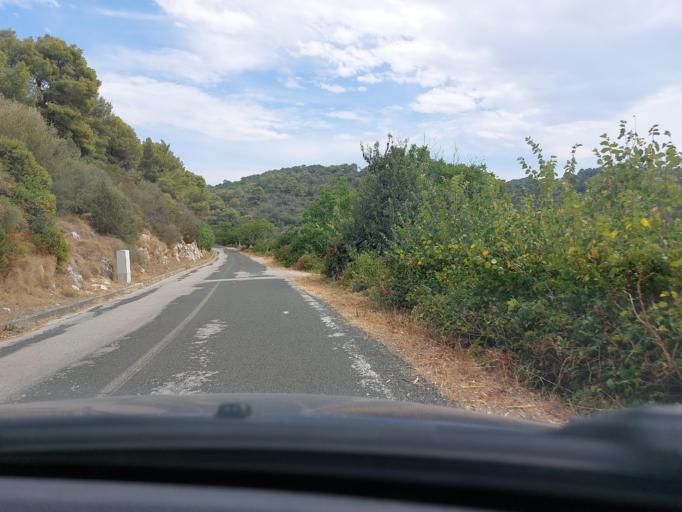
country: HR
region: Dubrovacko-Neretvanska
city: Smokvica
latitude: 42.7634
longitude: 16.8958
